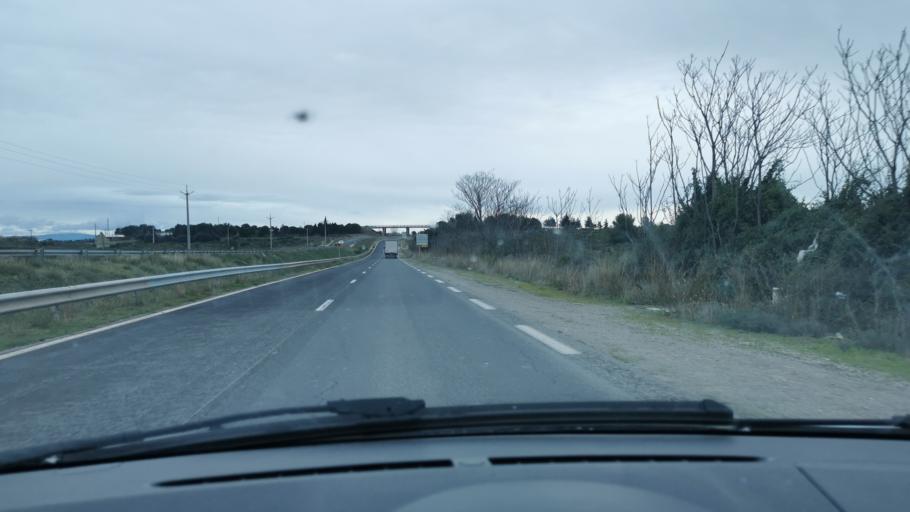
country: FR
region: Languedoc-Roussillon
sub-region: Departement de l'Herault
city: Saint-Jean-de-Vedas
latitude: 43.5406
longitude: 3.8229
